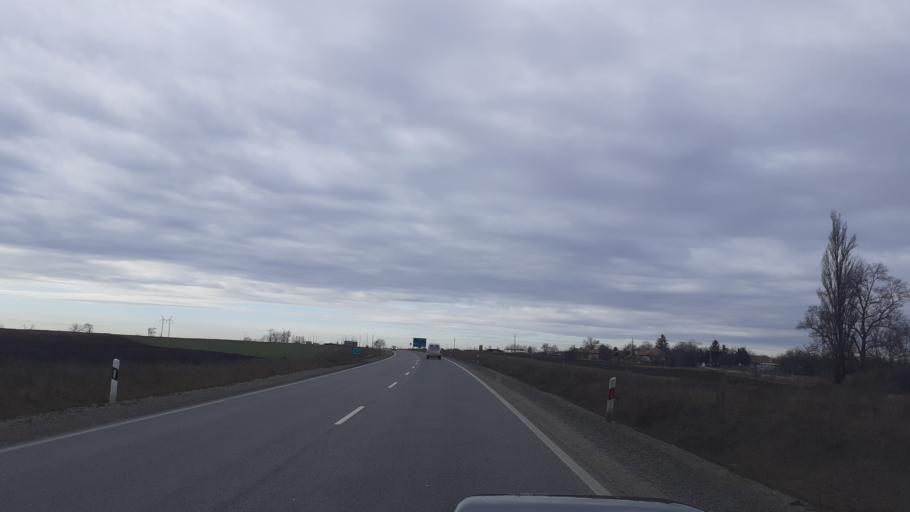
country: HU
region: Fejer
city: Sarosd
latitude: 47.1052
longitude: 18.6360
